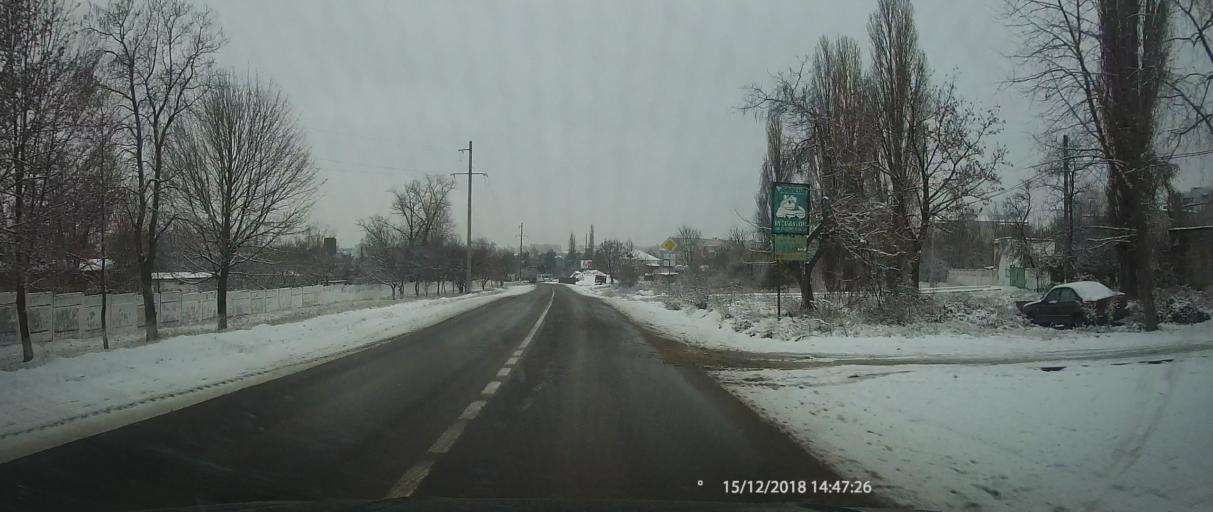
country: MD
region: Cahul
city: Cahul
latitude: 45.8937
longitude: 28.2063
